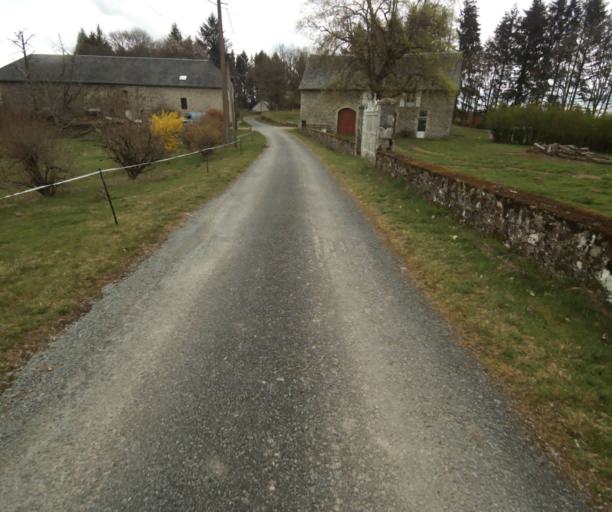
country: FR
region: Limousin
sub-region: Departement de la Correze
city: Correze
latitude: 45.3599
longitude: 1.9282
